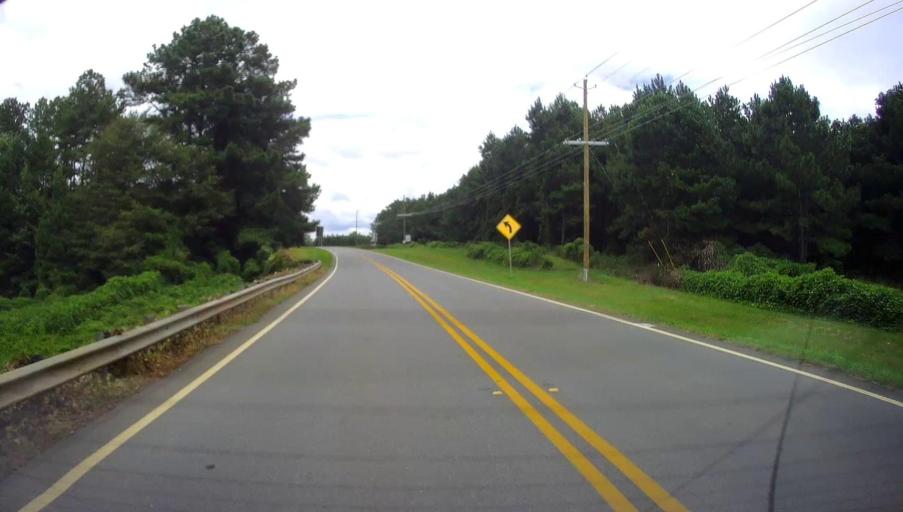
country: US
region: Georgia
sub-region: Schley County
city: Ellaville
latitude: 32.2406
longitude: -84.2925
